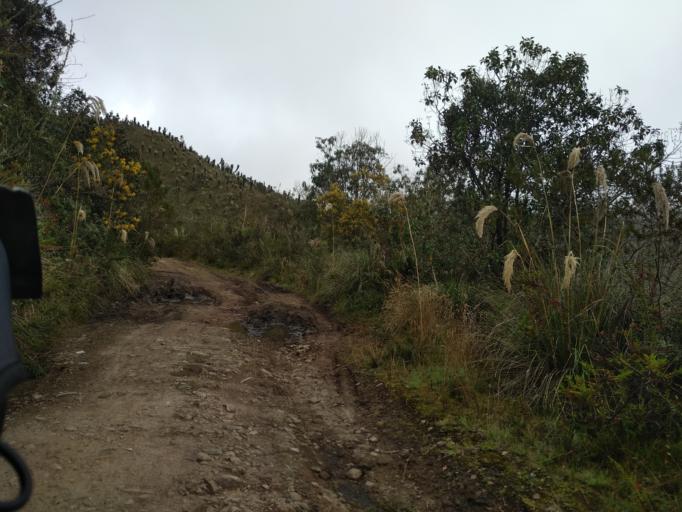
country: EC
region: Carchi
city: San Gabriel
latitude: 0.6956
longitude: -77.8472
